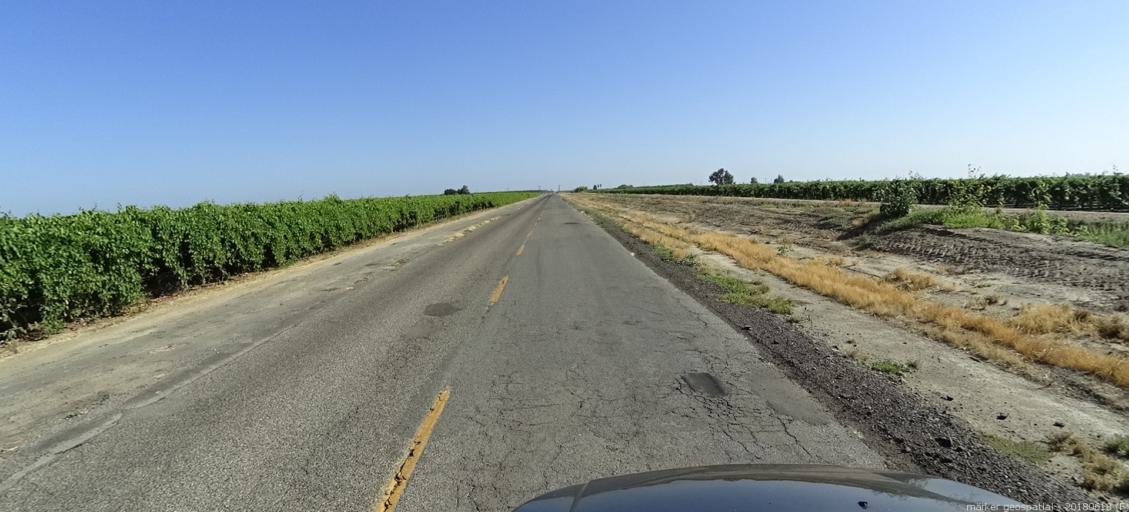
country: US
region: California
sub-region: Madera County
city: Parkwood
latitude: 36.8888
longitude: -120.1286
